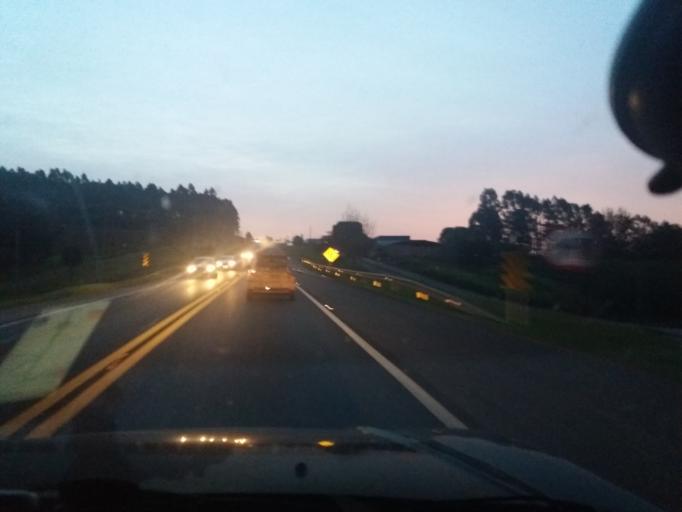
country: BR
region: Sao Paulo
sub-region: Itapeva
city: Itapeva
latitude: -23.9771
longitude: -48.8520
